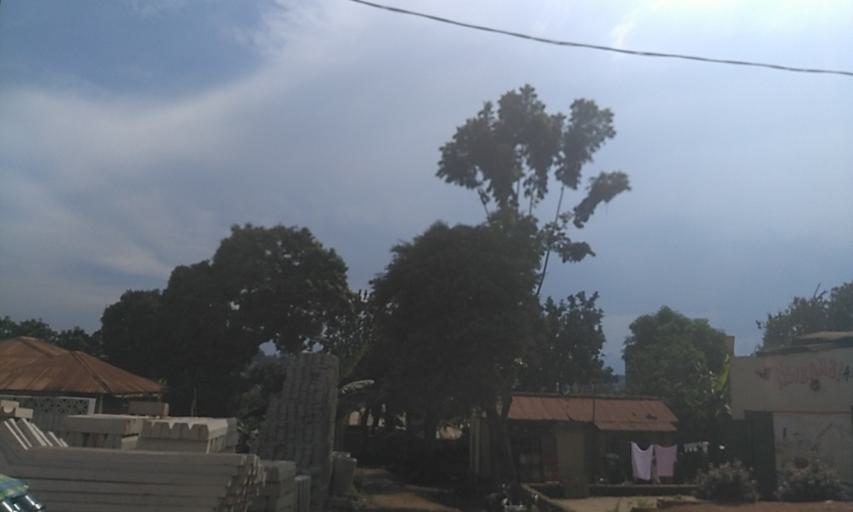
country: UG
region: Central Region
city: Kampala Central Division
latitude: 0.3055
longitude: 32.5189
